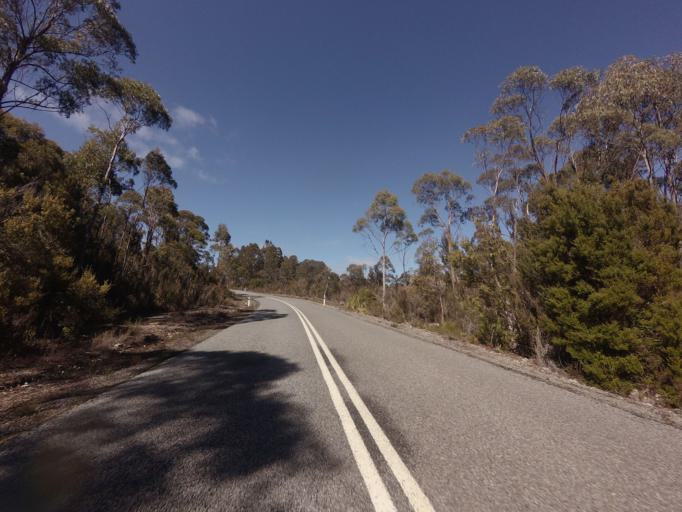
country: AU
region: Tasmania
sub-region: Huon Valley
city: Geeveston
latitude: -42.7699
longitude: 146.3967
